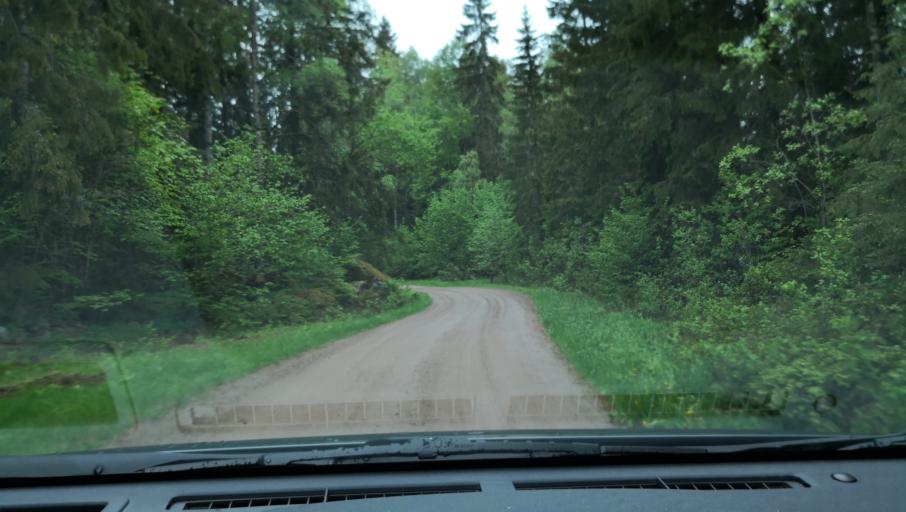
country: SE
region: Uppsala
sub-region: Enkopings Kommun
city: Orsundsbro
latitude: 59.9175
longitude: 17.3477
